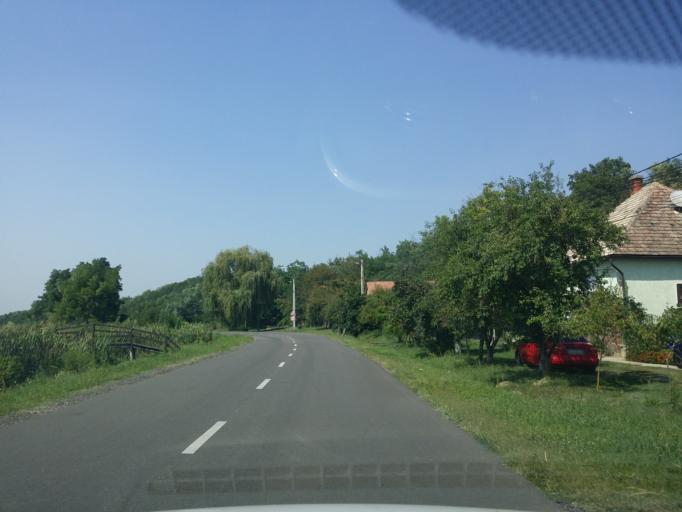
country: HU
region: Tolna
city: Pincehely
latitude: 46.6151
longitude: 18.4210
